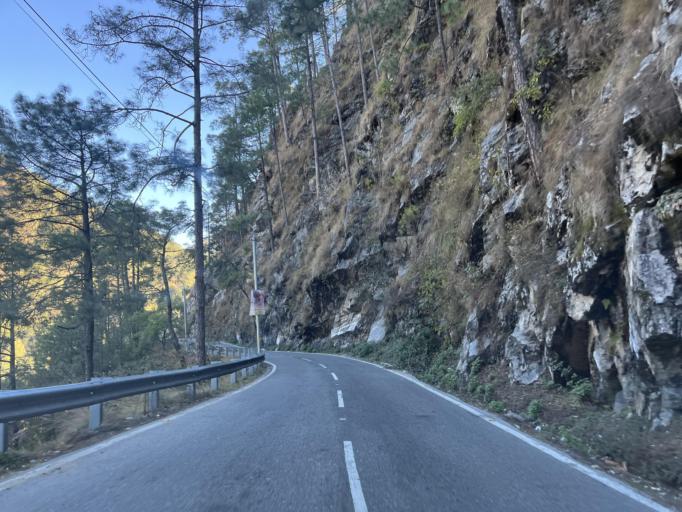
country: IN
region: Uttarakhand
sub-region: Naini Tal
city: Bhowali
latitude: 29.4035
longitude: 79.5101
